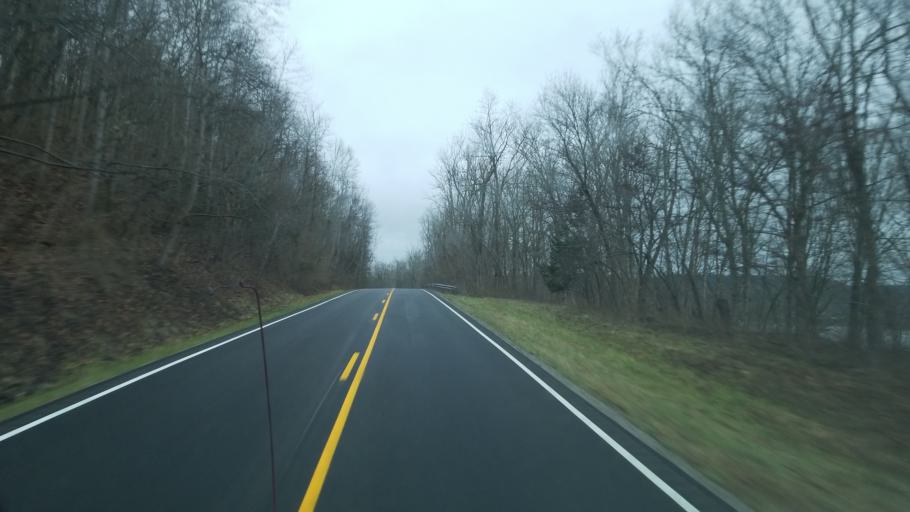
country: US
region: Kentucky
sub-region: Bracken County
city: Augusta
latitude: 38.7784
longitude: -83.9440
